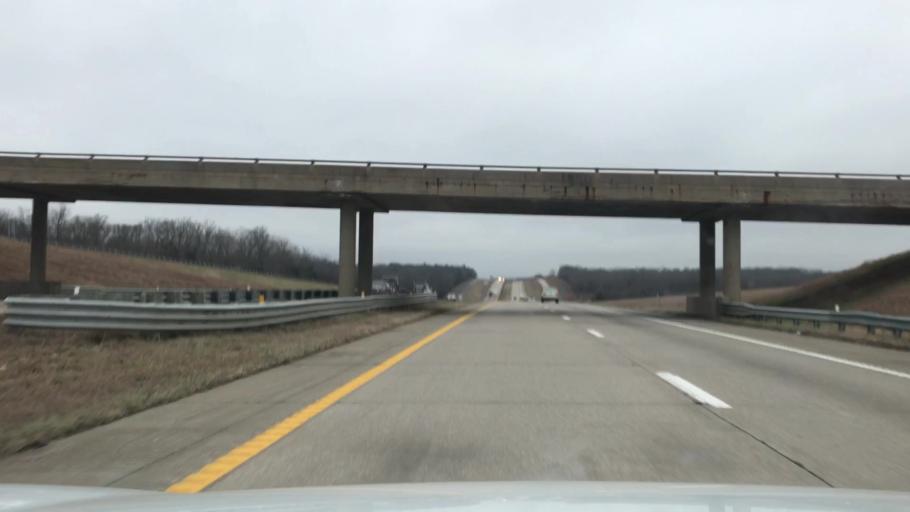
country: US
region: Missouri
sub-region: Crawford County
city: Bourbon
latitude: 38.1202
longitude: -91.3143
